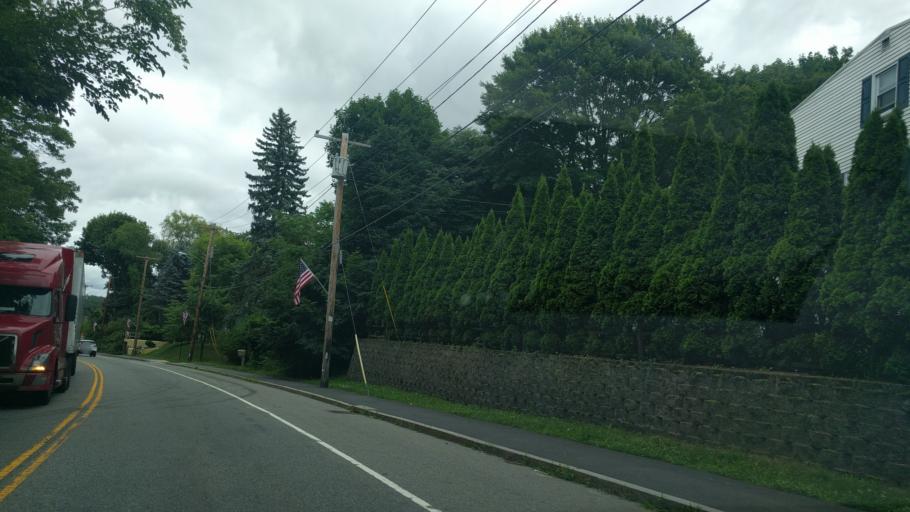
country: US
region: Massachusetts
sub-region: Worcester County
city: Worcester
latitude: 42.2358
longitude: -71.8002
